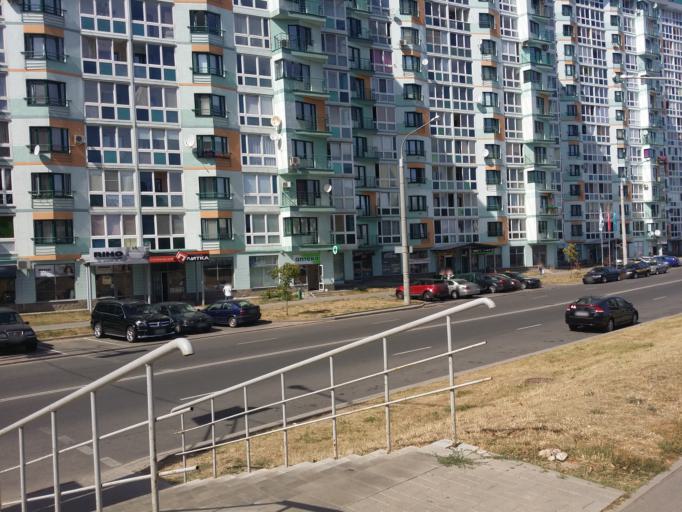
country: BY
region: Minsk
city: Minsk
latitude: 53.9419
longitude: 27.5976
